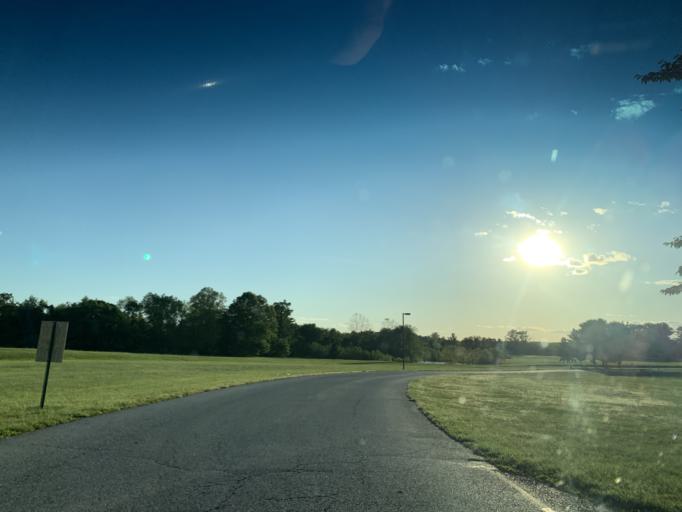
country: US
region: Maryland
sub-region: Cecil County
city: Elkton
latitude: 39.6468
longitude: -75.8073
